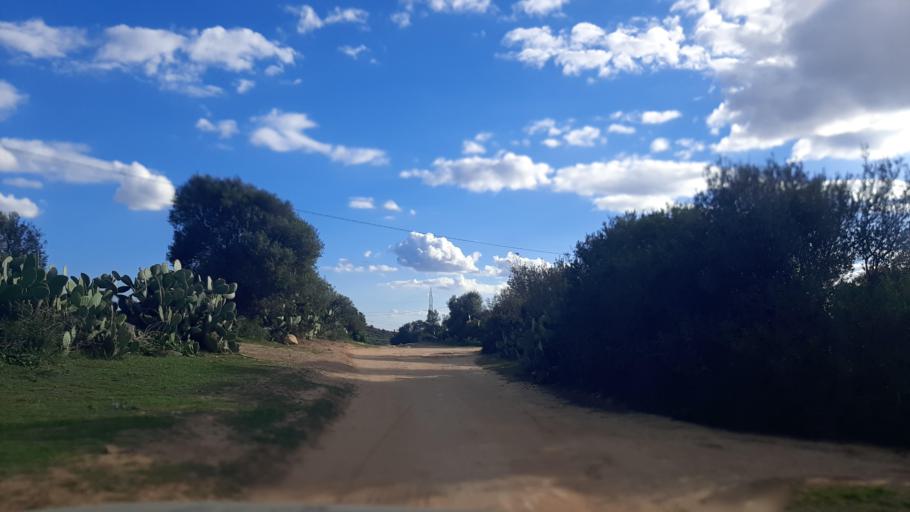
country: TN
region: Nabul
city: Bu `Urqub
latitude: 36.4428
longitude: 10.5066
